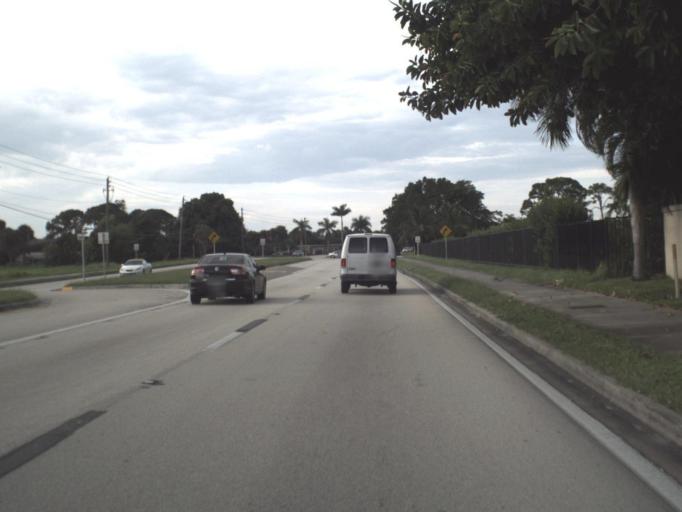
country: US
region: Florida
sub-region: Lee County
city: Cypress Lake
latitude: 26.5440
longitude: -81.9152
